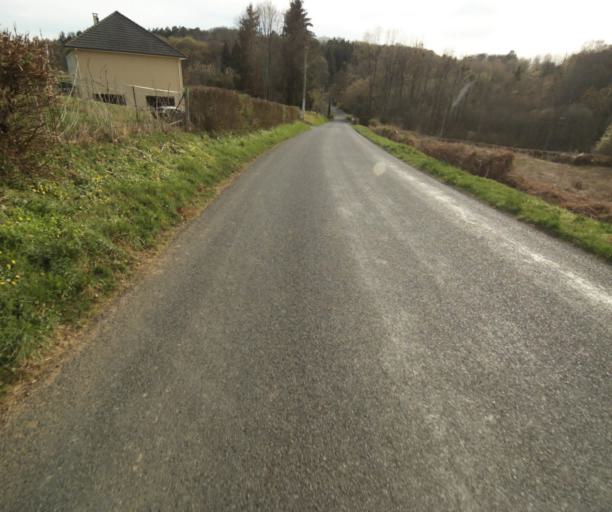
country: FR
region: Limousin
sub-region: Departement de la Correze
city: Naves
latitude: 45.3152
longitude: 1.7580
